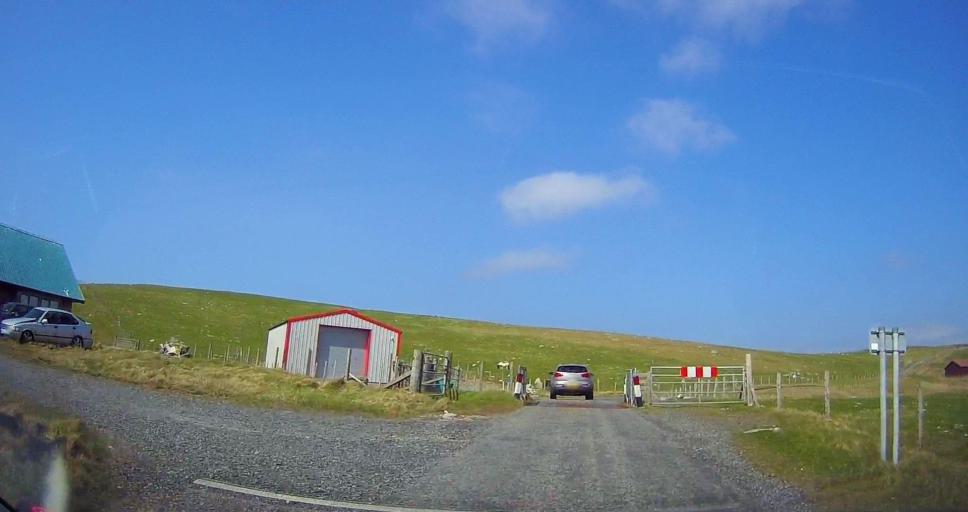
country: GB
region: Scotland
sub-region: Shetland Islands
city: Sandwick
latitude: 60.0702
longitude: -1.3403
